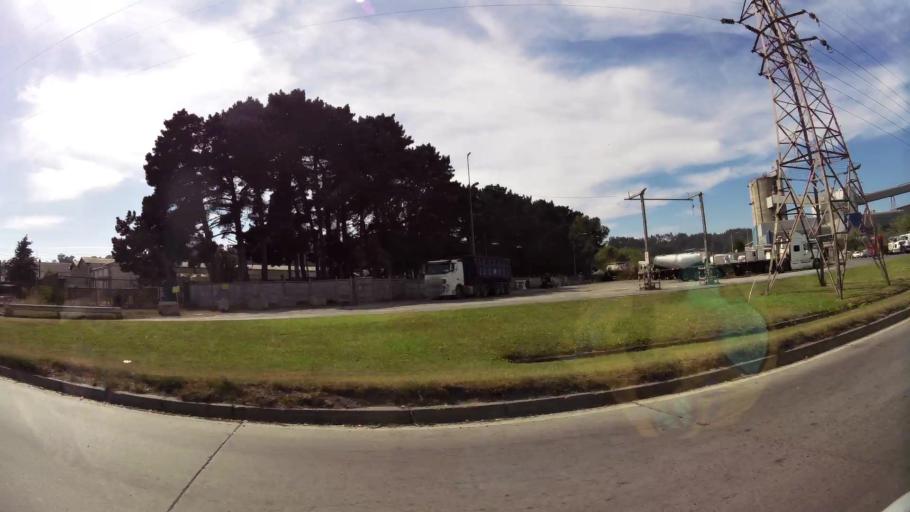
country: CL
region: Biobio
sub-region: Provincia de Concepcion
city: Talcahuano
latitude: -36.7409
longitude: -73.1191
